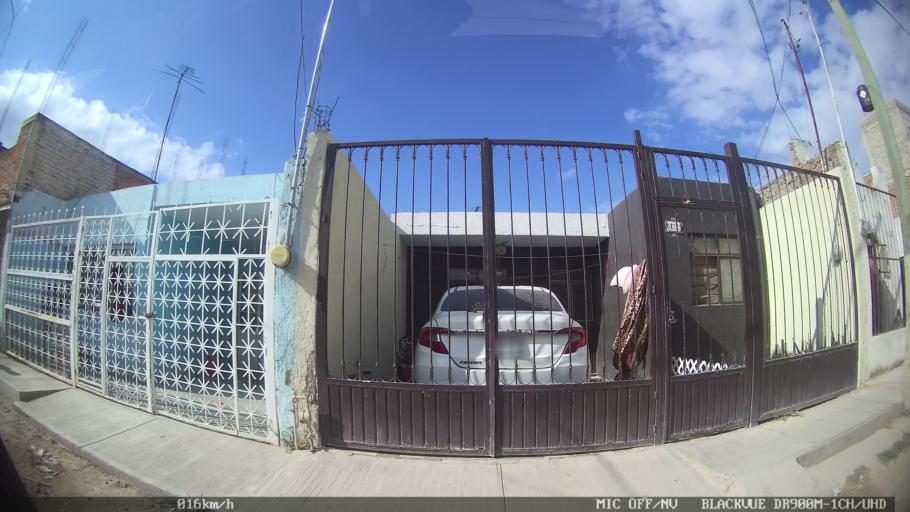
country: MX
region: Jalisco
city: Tonala
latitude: 20.6570
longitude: -103.2498
